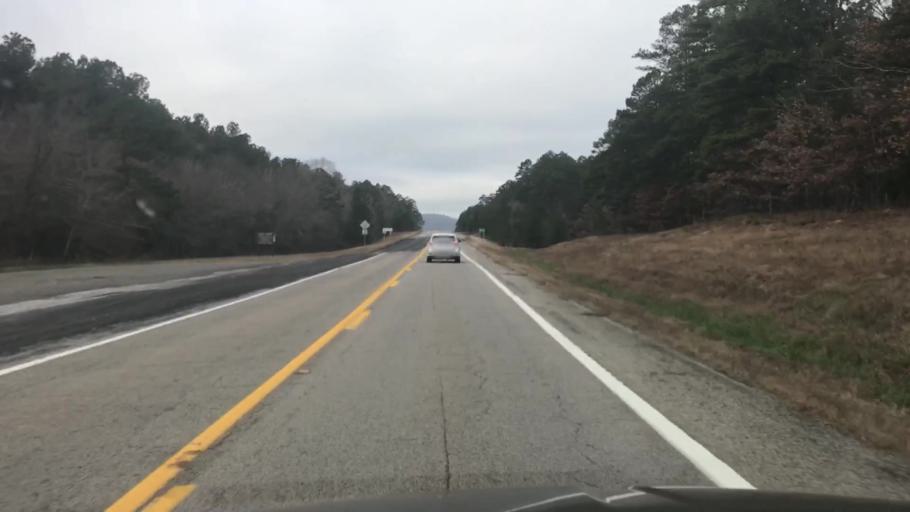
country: US
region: Arkansas
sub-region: Montgomery County
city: Mount Ida
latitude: 34.6873
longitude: -93.8776
